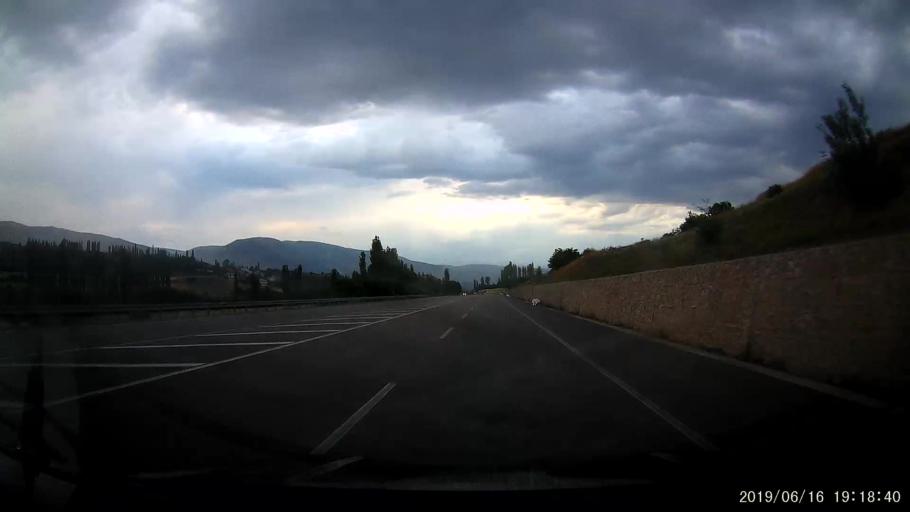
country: TR
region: Sivas
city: Akincilar
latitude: 40.0952
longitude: 38.4511
